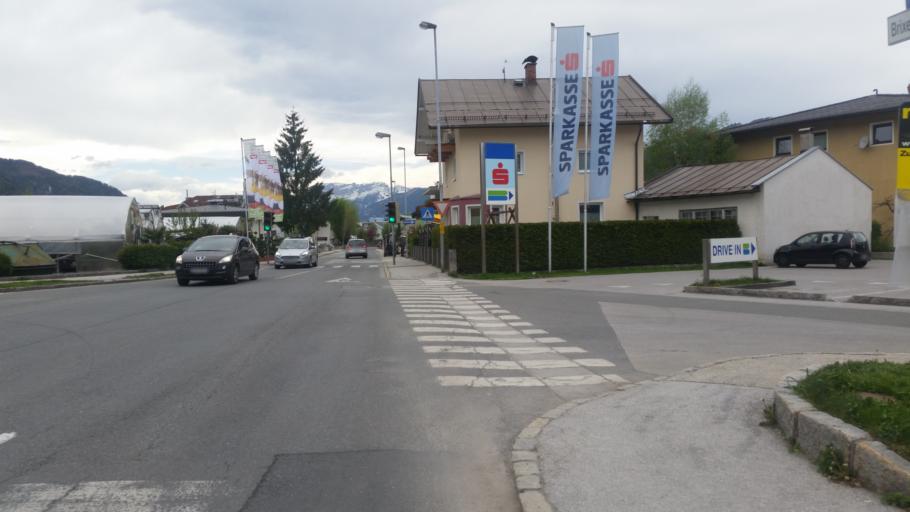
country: AT
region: Tyrol
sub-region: Politischer Bezirk Kufstein
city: Worgl
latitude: 47.4861
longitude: 12.0721
